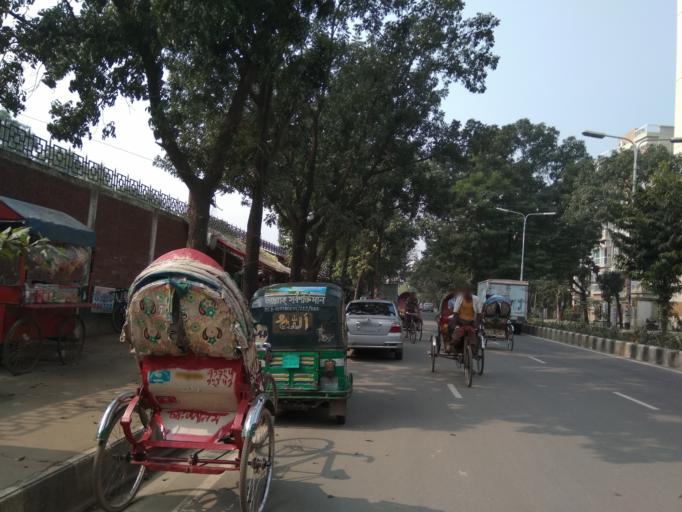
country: BD
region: Dhaka
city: Tungi
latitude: 23.8612
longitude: 90.3954
